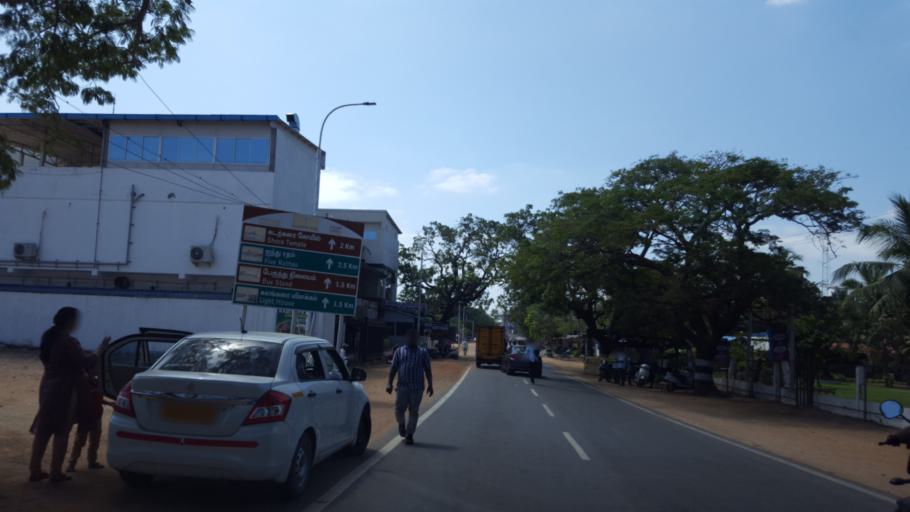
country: IN
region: Tamil Nadu
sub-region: Kancheepuram
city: Mamallapuram
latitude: 12.6268
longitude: 80.1944
